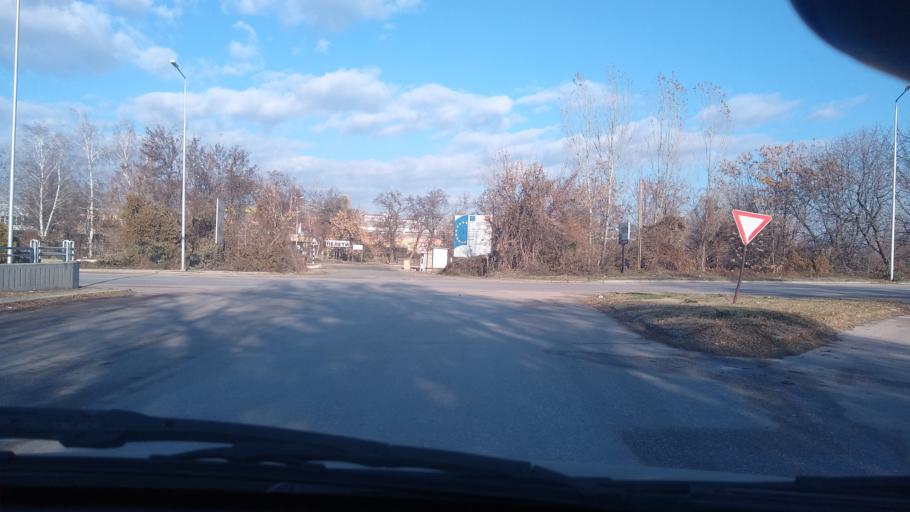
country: MK
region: Bitola
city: Bitola
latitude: 41.0130
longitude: 21.3483
